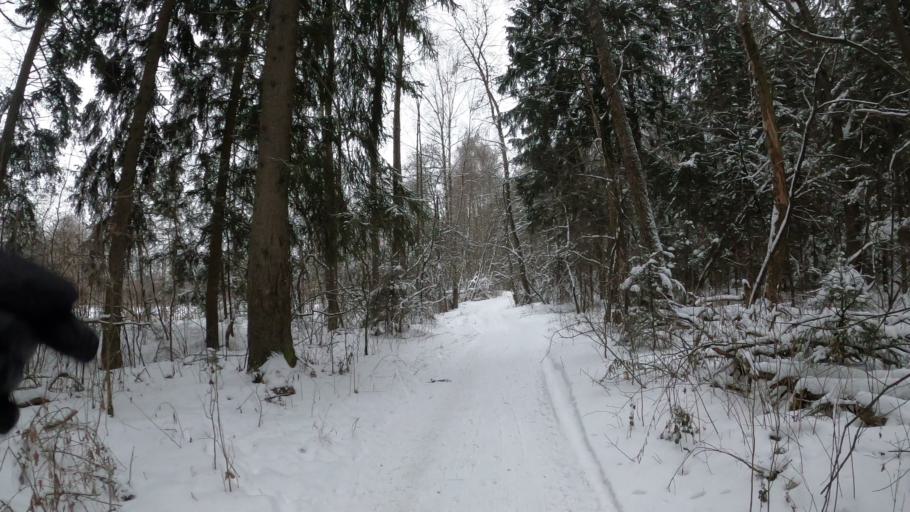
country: RU
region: Moskovskaya
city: Firsanovka
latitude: 55.9377
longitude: 37.2200
